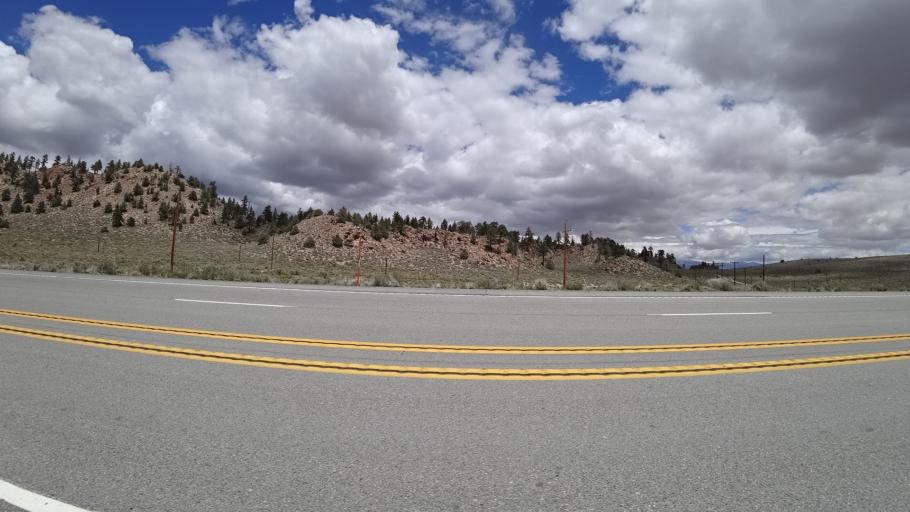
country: US
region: California
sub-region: Inyo County
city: West Bishop
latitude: 37.5505
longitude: -118.6406
